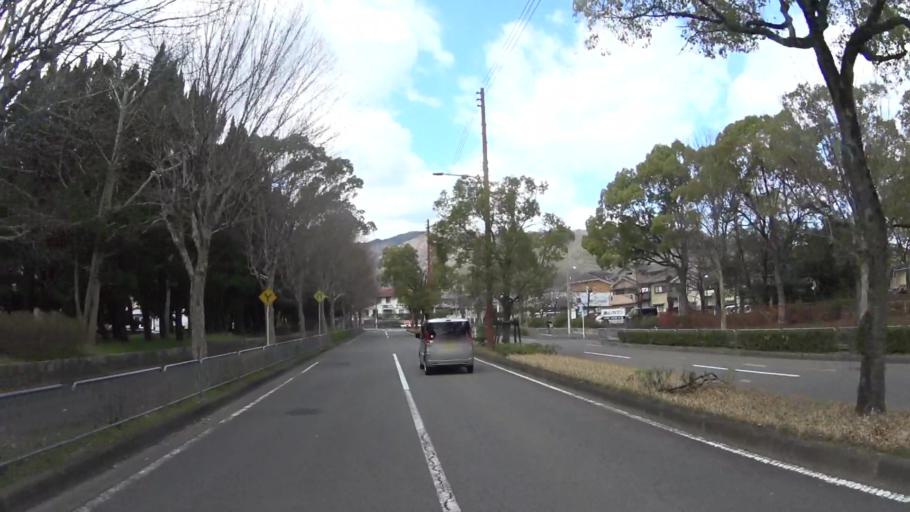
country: JP
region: Kyoto
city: Muko
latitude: 34.9560
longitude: 135.6717
